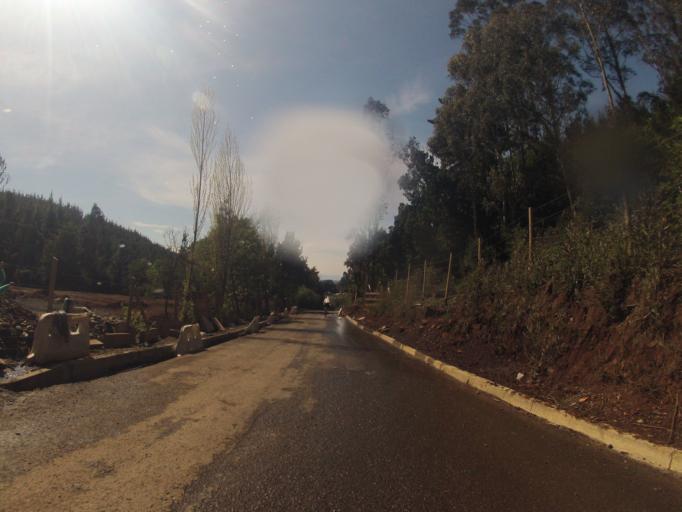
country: CL
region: Araucania
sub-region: Provincia de Cautin
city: Temuco
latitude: -38.6896
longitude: -72.5567
